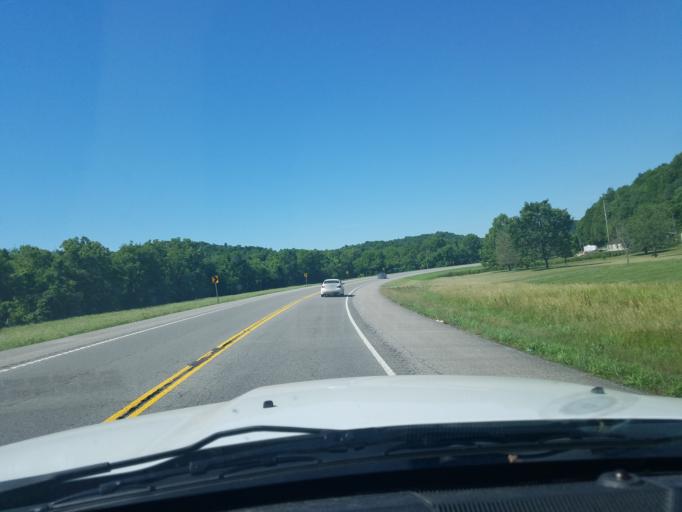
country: US
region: Tennessee
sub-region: Sumner County
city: Westmoreland
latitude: 36.5069
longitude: -86.2667
